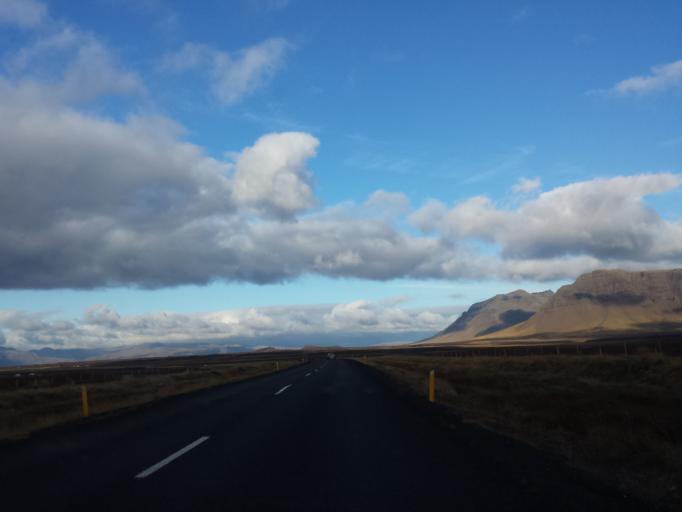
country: IS
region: West
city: Borgarnes
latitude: 64.7261
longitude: -22.1761
